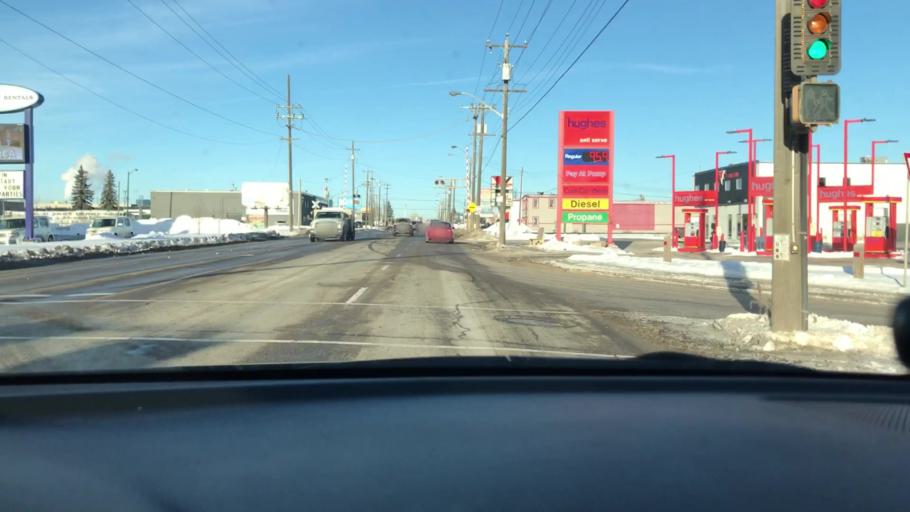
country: CA
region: Alberta
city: Edmonton
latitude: 53.4959
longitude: -113.4861
